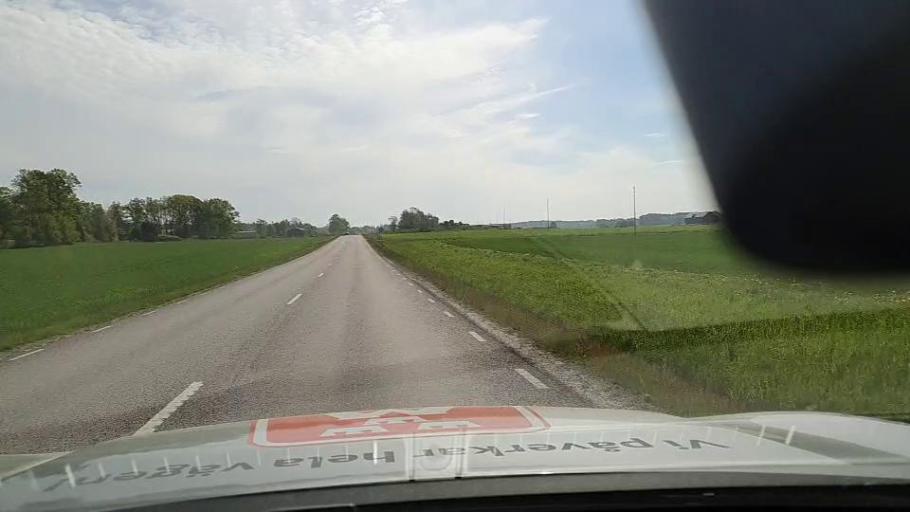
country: SE
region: Soedermanland
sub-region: Eskilstuna Kommun
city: Eskilstuna
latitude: 59.3182
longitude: 16.5441
